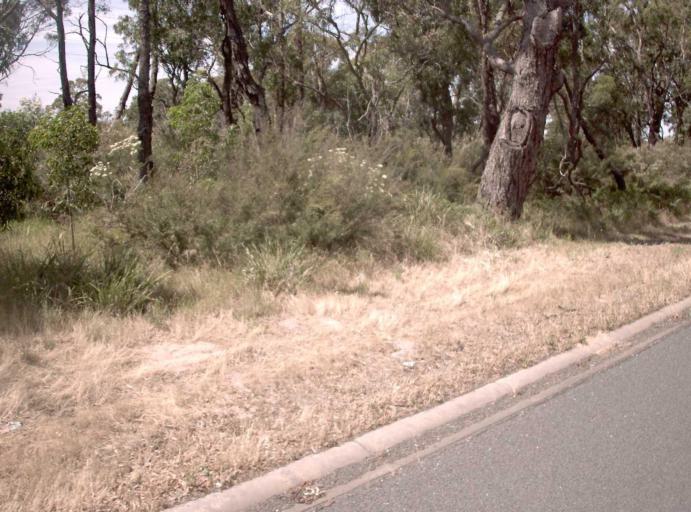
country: AU
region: Victoria
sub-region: Wellington
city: Sale
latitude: -37.9421
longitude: 147.1416
